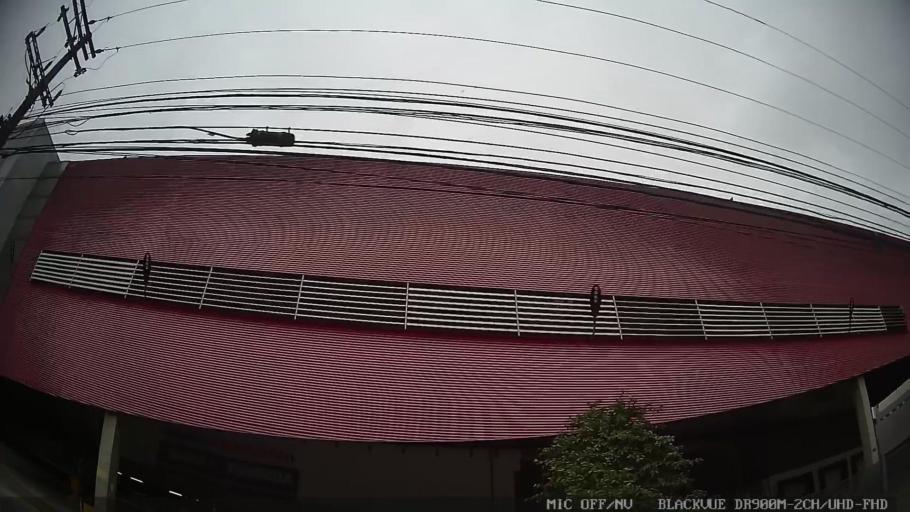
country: BR
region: Sao Paulo
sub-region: Sao Paulo
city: Sao Paulo
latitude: -23.5103
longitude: -46.7007
